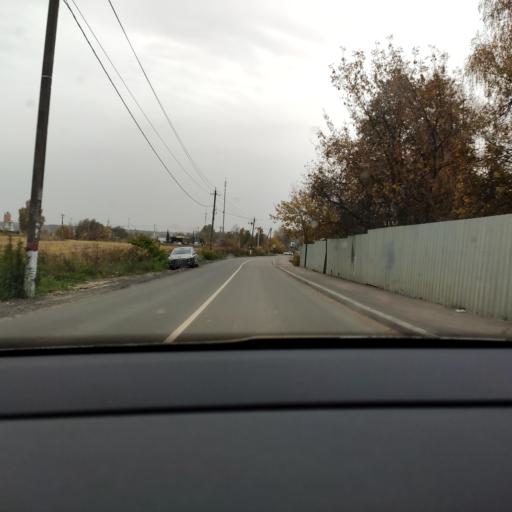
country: RU
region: Moskovskaya
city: Ivanteyevka
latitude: 55.9650
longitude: 37.9461
